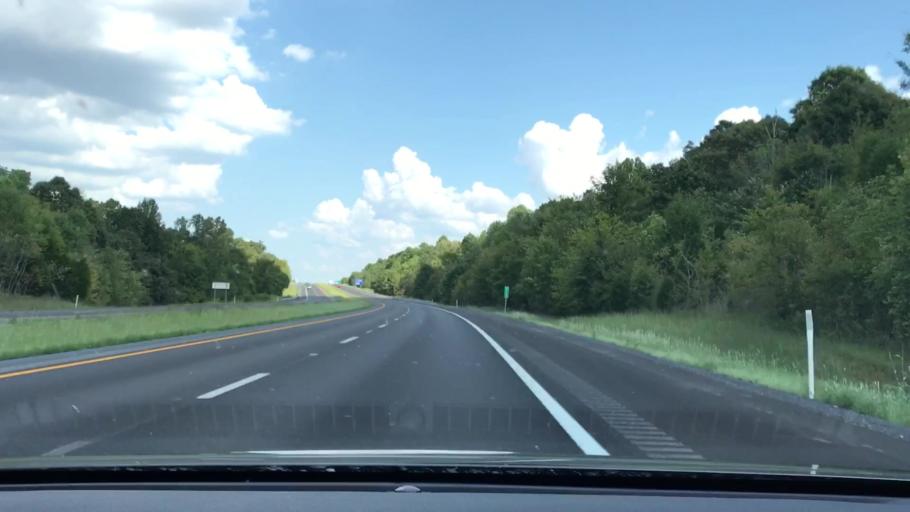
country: US
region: Kentucky
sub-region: Lyon County
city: Eddyville
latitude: 37.0962
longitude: -88.0429
